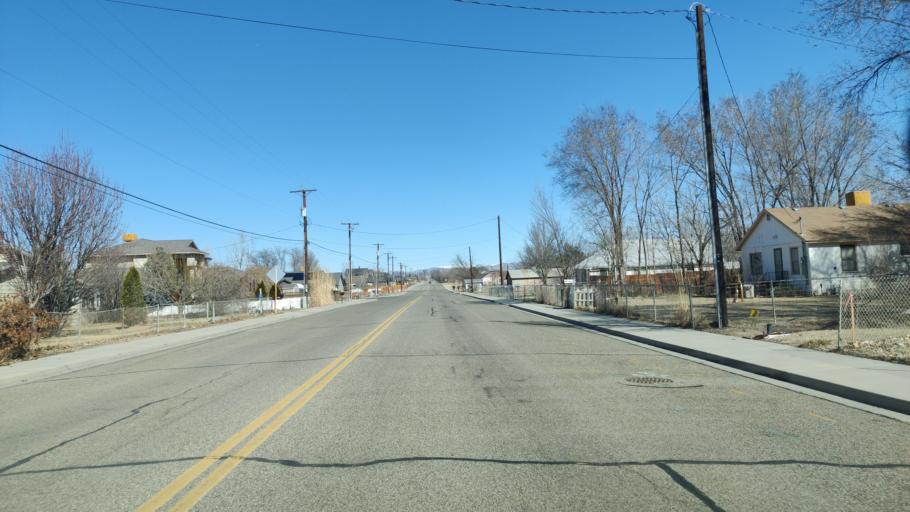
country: US
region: Colorado
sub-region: Mesa County
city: Fruita
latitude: 39.1711
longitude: -108.7197
